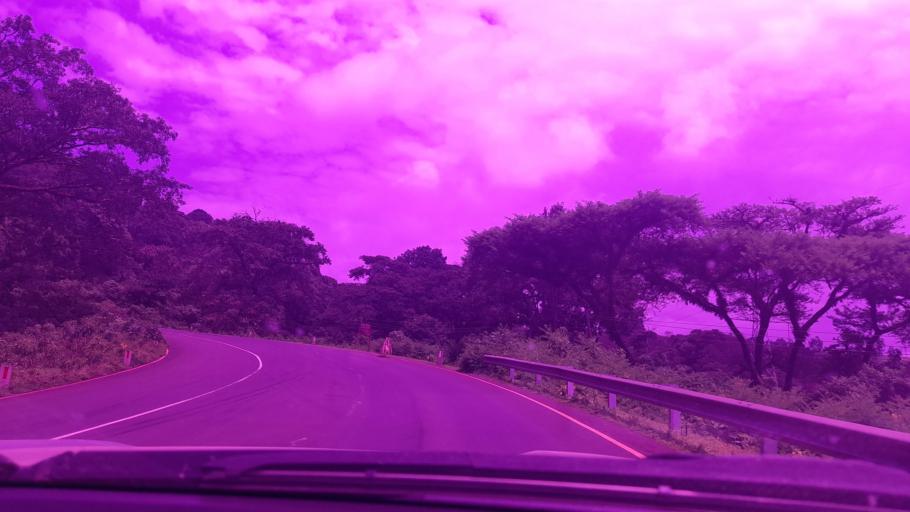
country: ET
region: Oromiya
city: Metu
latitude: 8.3382
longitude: 35.7453
